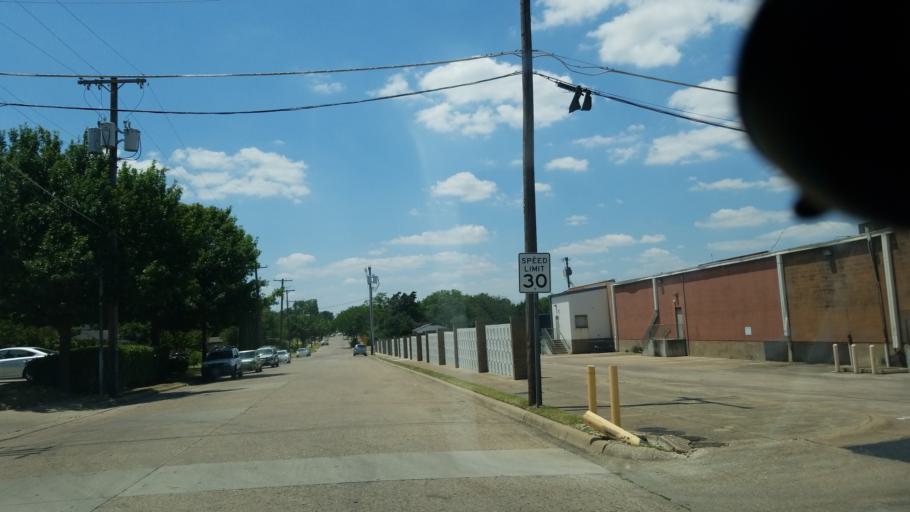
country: US
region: Texas
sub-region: Dallas County
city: Cockrell Hill
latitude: 32.7185
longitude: -96.8577
